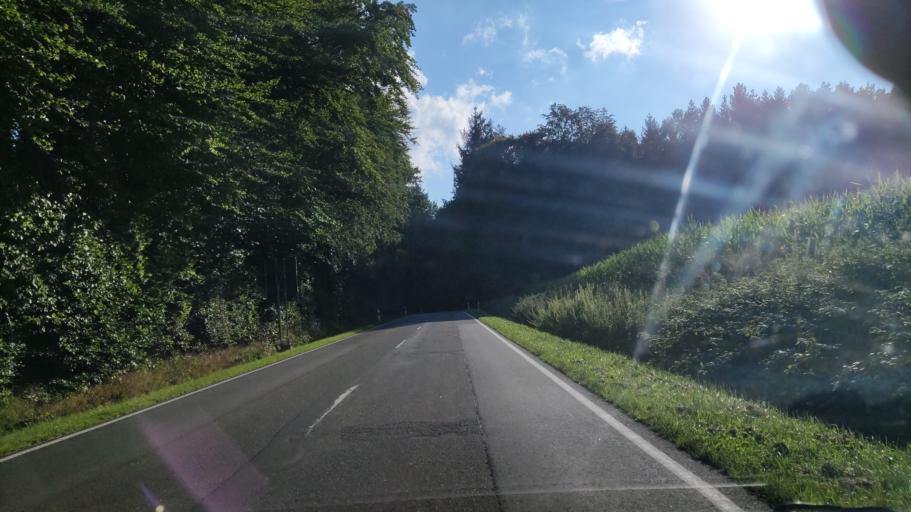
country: DE
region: Schleswig-Holstein
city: Aukrug
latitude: 54.0760
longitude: 9.7737
